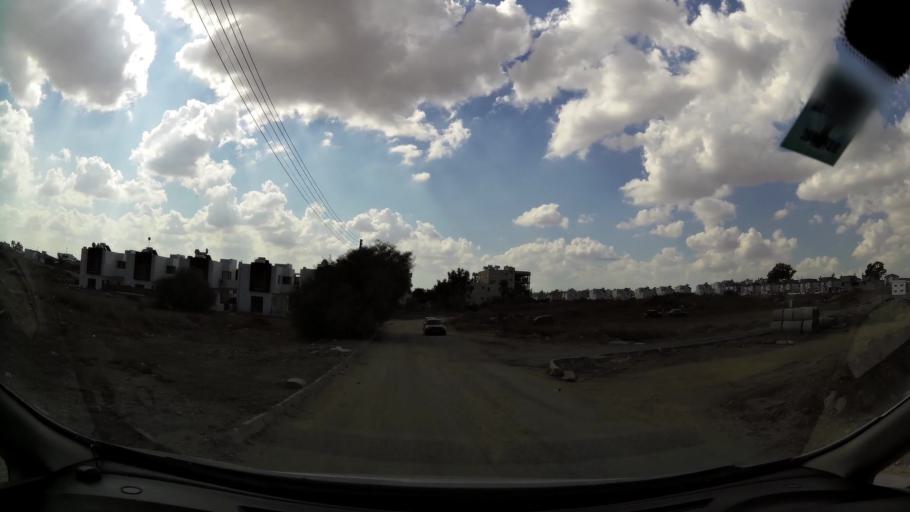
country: CY
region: Lefkosia
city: Nicosia
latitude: 35.2217
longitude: 33.3746
